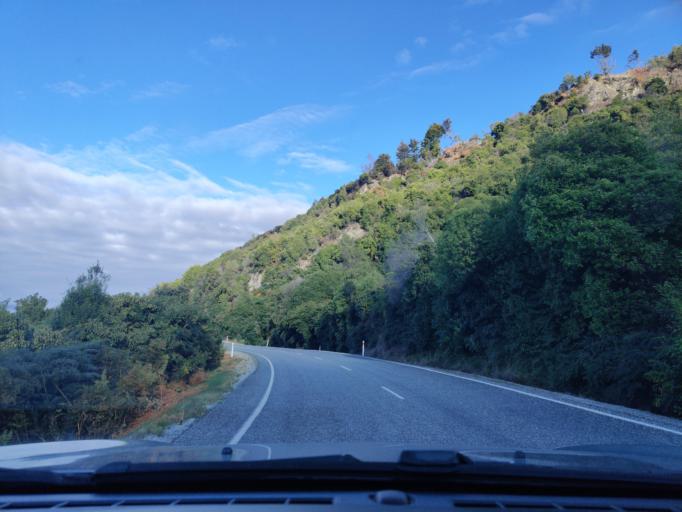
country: NZ
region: Otago
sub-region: Queenstown-Lakes District
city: Queenstown
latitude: -45.0551
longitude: 168.6057
